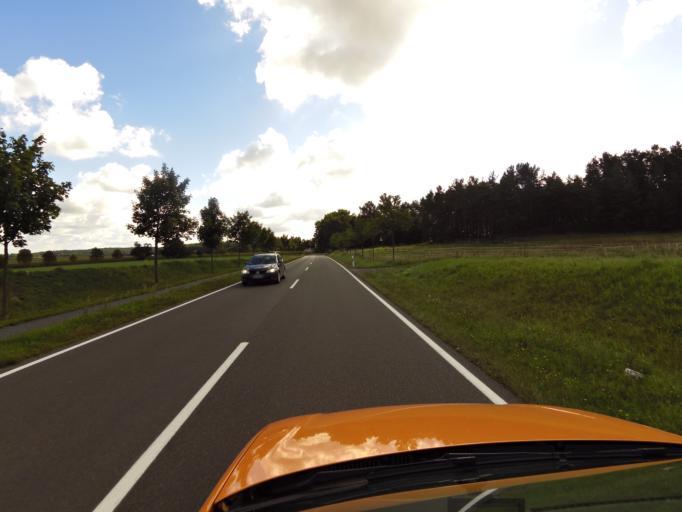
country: DE
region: Brandenburg
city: Michendorf
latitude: 52.2745
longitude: 13.0718
